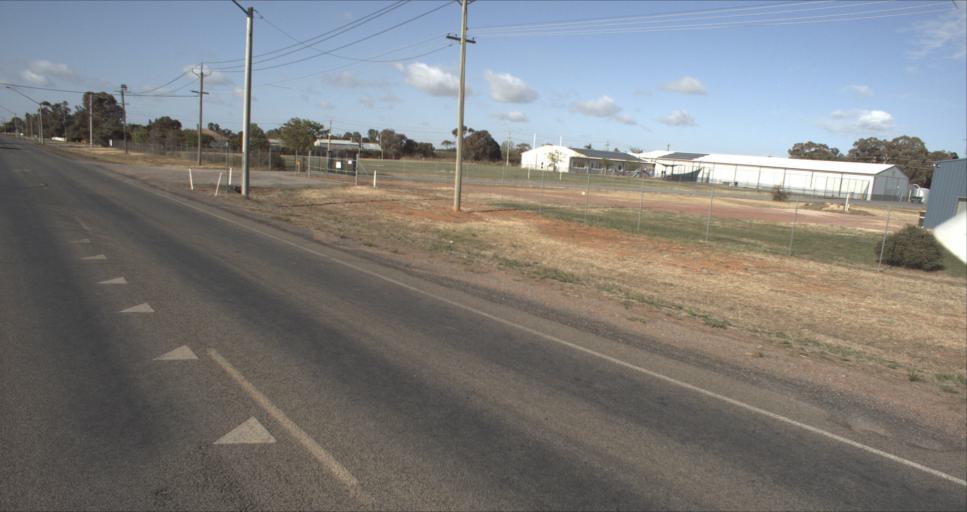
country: AU
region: New South Wales
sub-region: Leeton
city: Leeton
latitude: -34.5635
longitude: 146.3929
